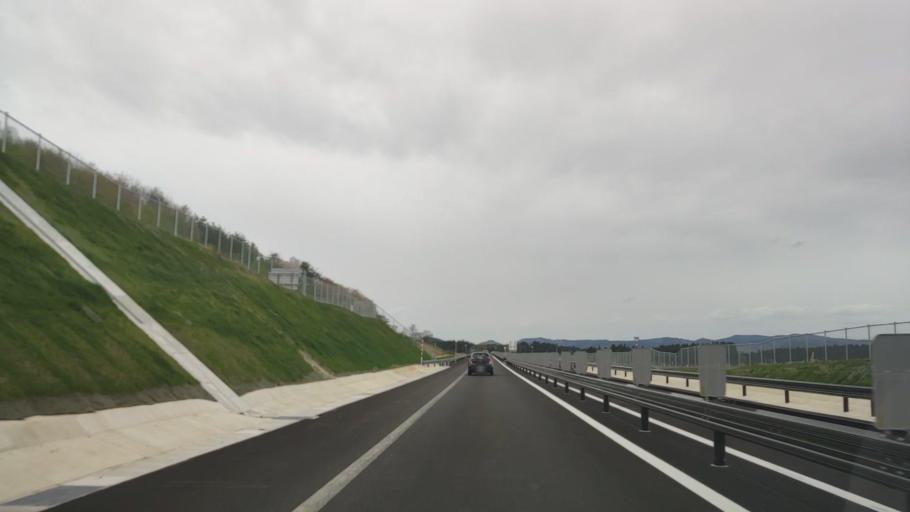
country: JP
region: Akita
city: Takanosu
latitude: 40.1995
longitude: 140.3637
